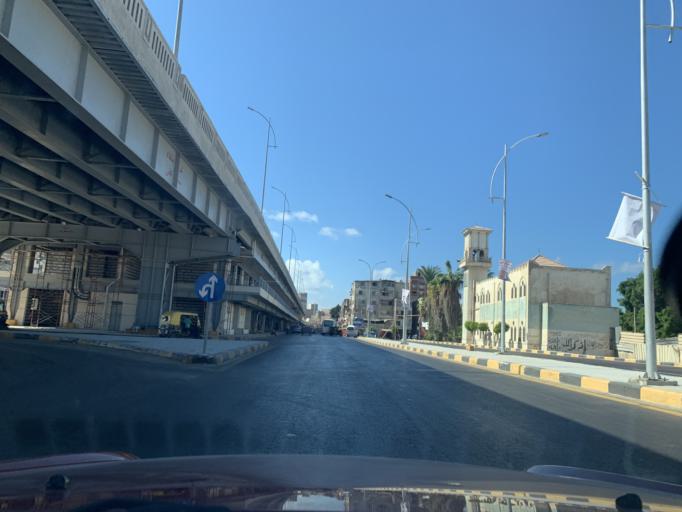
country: EG
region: Alexandria
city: Alexandria
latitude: 31.2237
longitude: 29.9847
